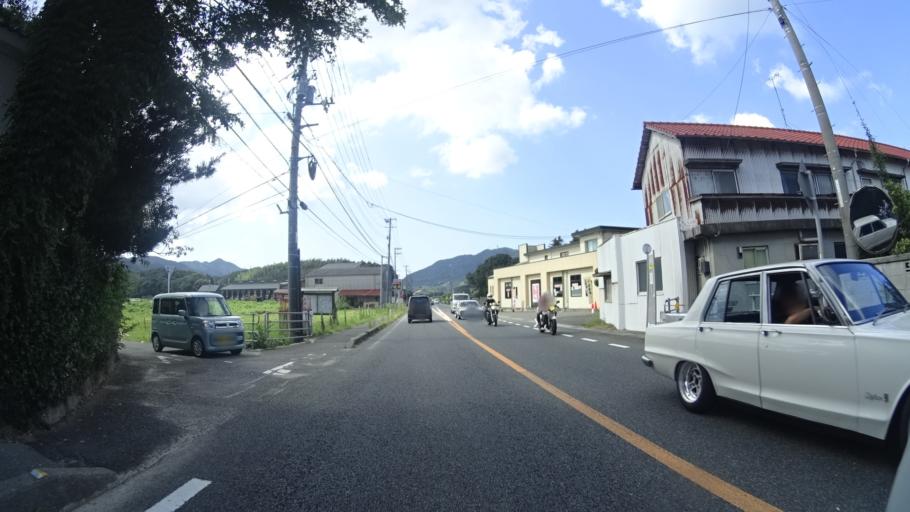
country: JP
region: Yamaguchi
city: Shimonoseki
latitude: 34.1237
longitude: 130.9126
